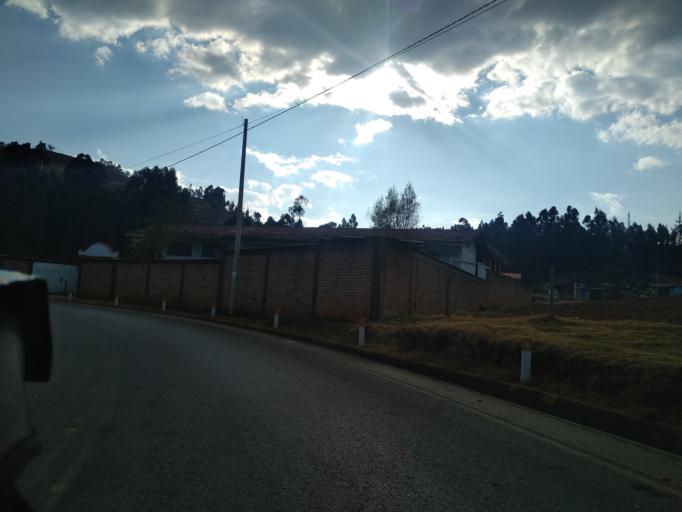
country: PE
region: Cajamarca
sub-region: Provincia de Cajamarca
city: Llacanora
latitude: -7.1436
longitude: -78.4101
